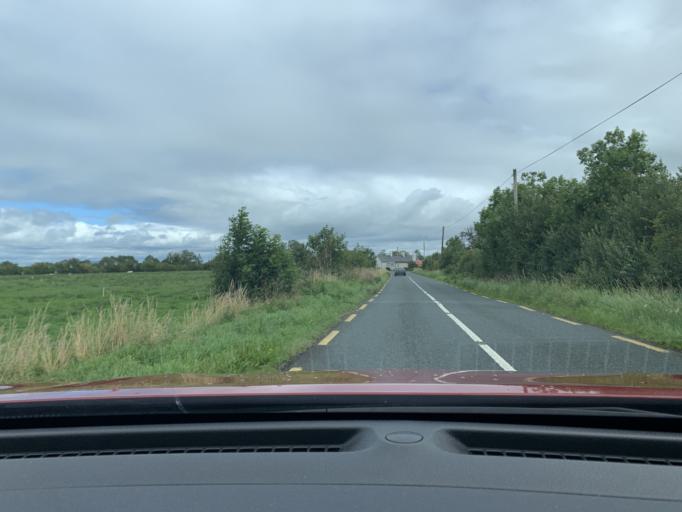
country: IE
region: Connaught
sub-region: County Leitrim
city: Carrick-on-Shannon
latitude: 53.8982
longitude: -8.1383
